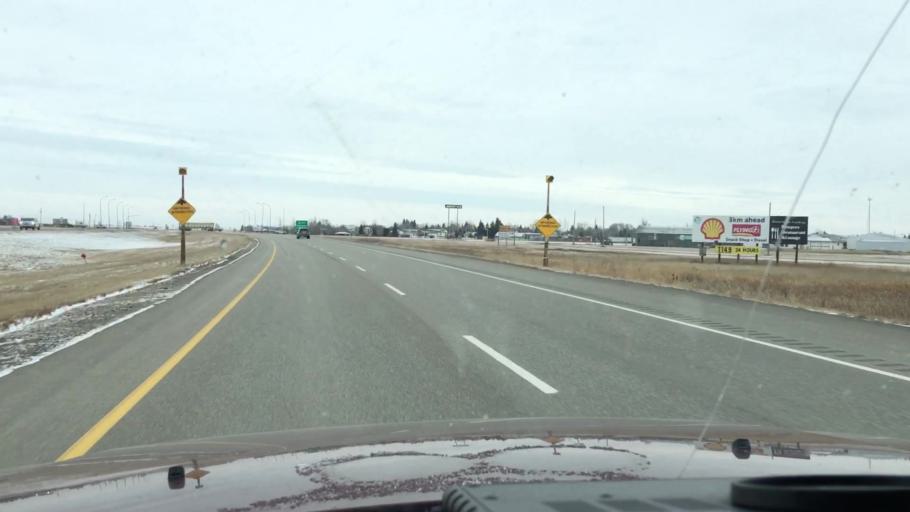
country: CA
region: Saskatchewan
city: Watrous
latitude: 51.2719
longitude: -106.0005
